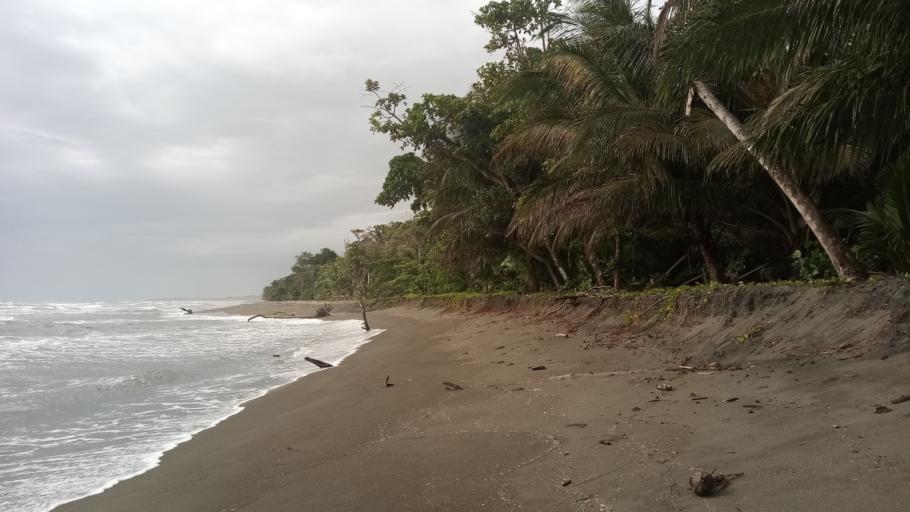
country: CR
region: Limon
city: Sixaola
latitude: 9.6133
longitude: -82.6186
